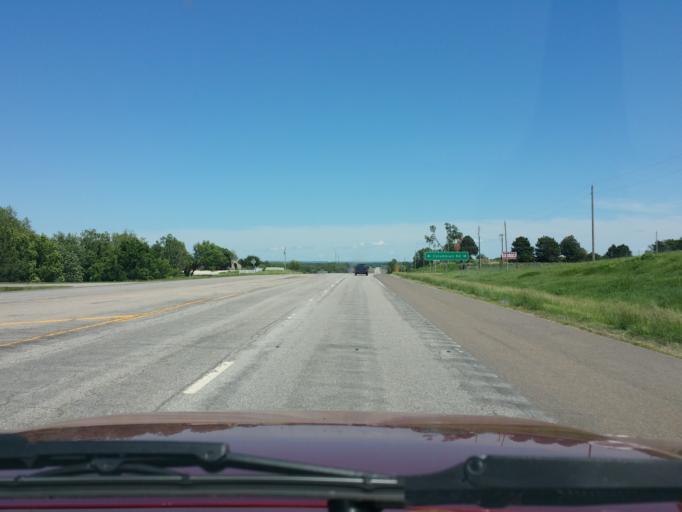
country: US
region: Kansas
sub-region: Pottawatomie County
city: Wamego
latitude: 39.2103
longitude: -96.3275
